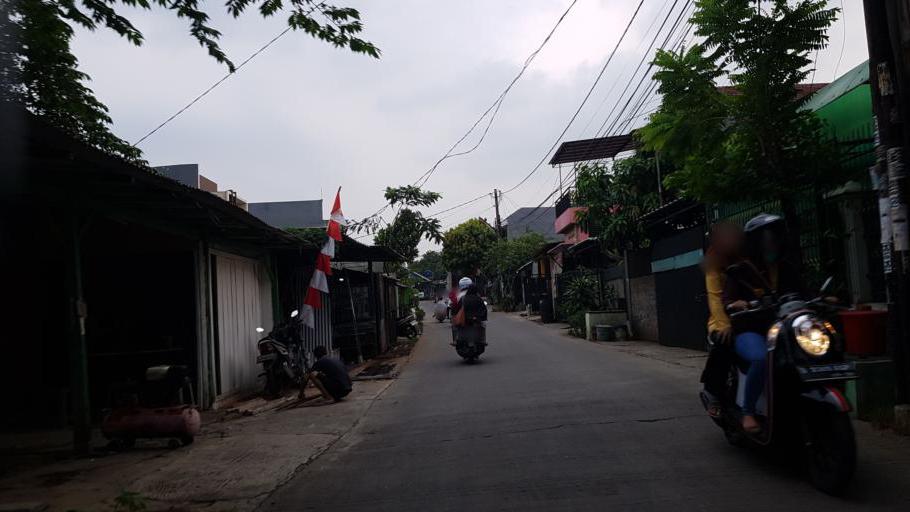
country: ID
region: West Java
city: Depok
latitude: -6.3731
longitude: 106.7955
